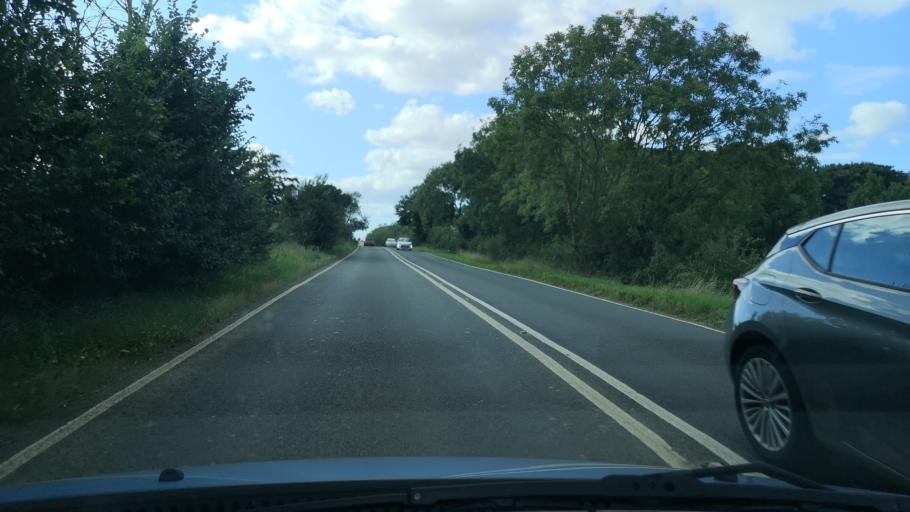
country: GB
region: England
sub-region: City and Borough of Wakefield
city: Badsworth
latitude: 53.6164
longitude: -1.3035
